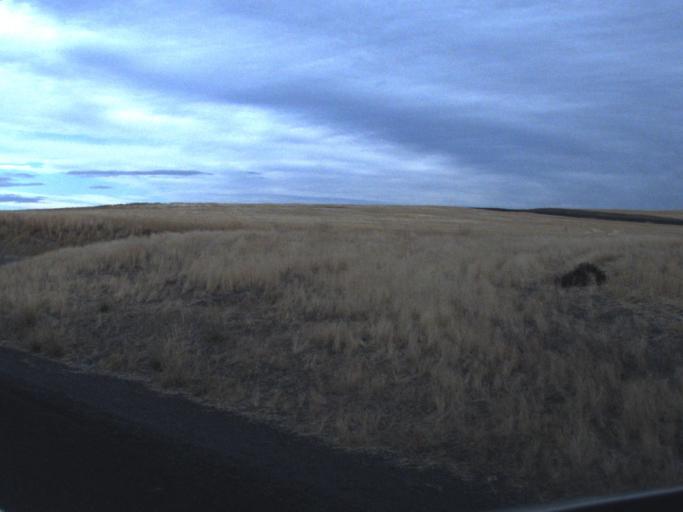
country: US
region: Washington
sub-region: Okanogan County
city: Coulee Dam
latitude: 47.7724
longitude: -118.7237
